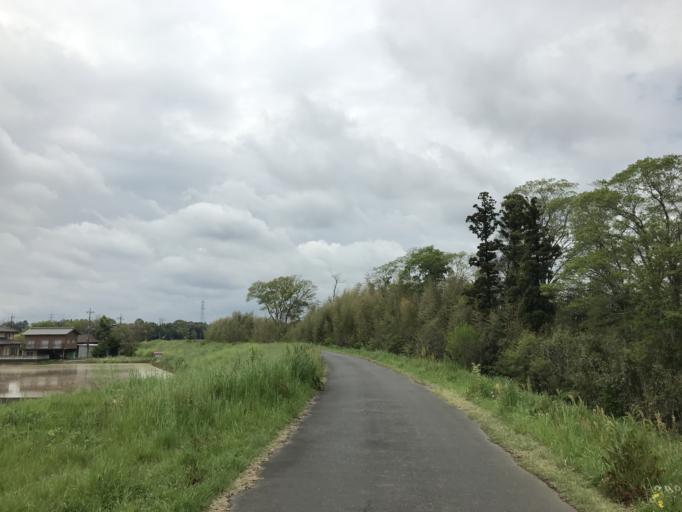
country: JP
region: Ibaraki
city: Moriya
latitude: 35.9737
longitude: 139.9995
